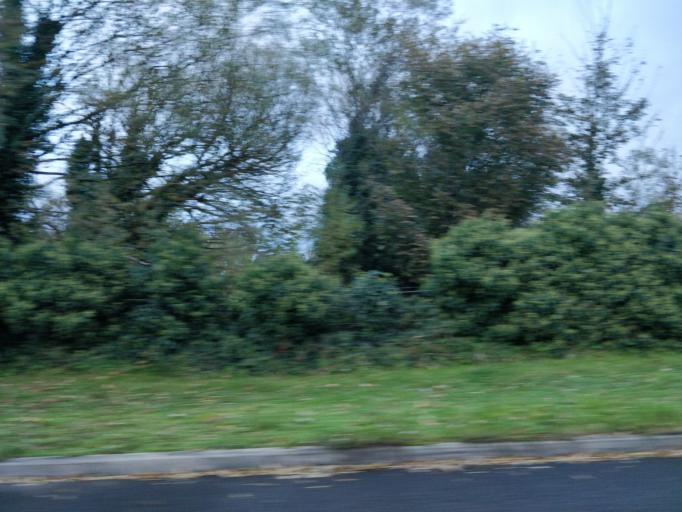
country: GB
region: England
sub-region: Sefton
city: Southport
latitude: 53.6622
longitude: -2.9866
